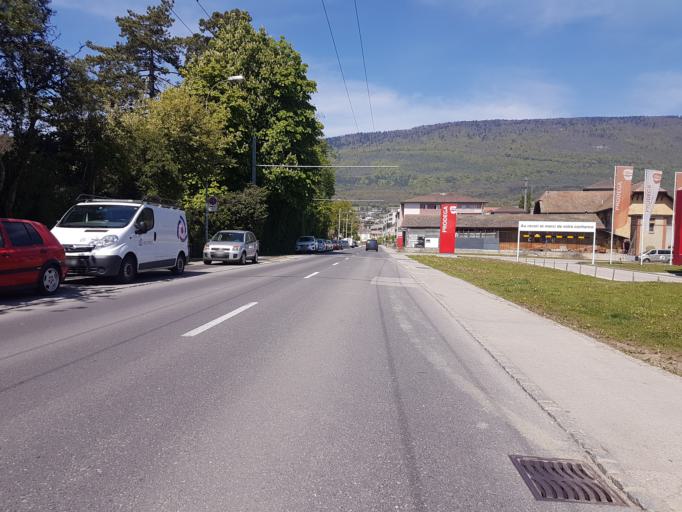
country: CH
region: Neuchatel
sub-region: Neuchatel District
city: Saint-Blaise
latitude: 47.0103
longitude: 6.9934
